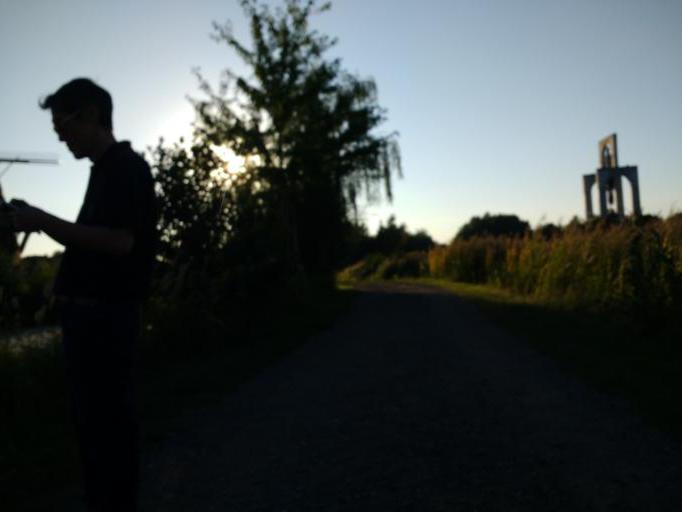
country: DE
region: Lower Saxony
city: Gifhorn
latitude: 52.4931
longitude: 10.5542
